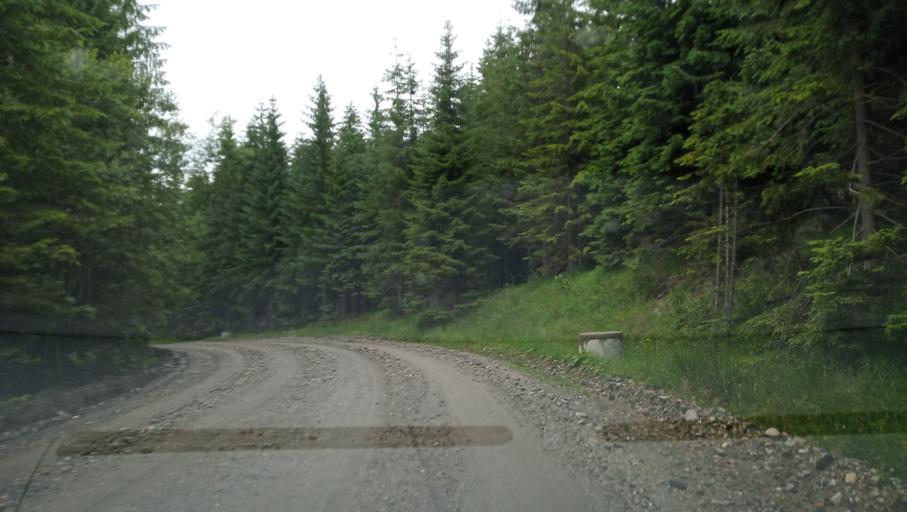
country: RO
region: Hunedoara
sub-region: Oras Petrila
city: Petrila
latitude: 45.4019
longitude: 23.5683
